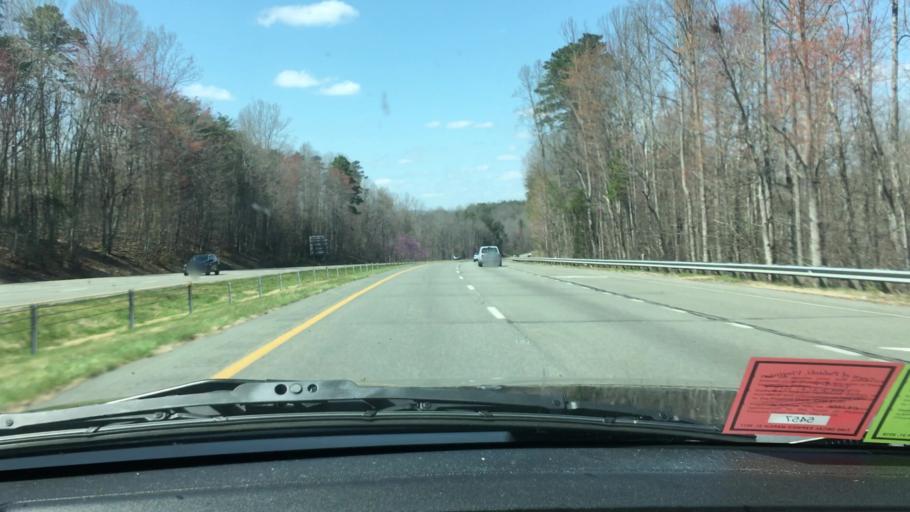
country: US
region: North Carolina
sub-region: Surry County
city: Pilot Mountain
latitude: 36.3792
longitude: -80.4880
